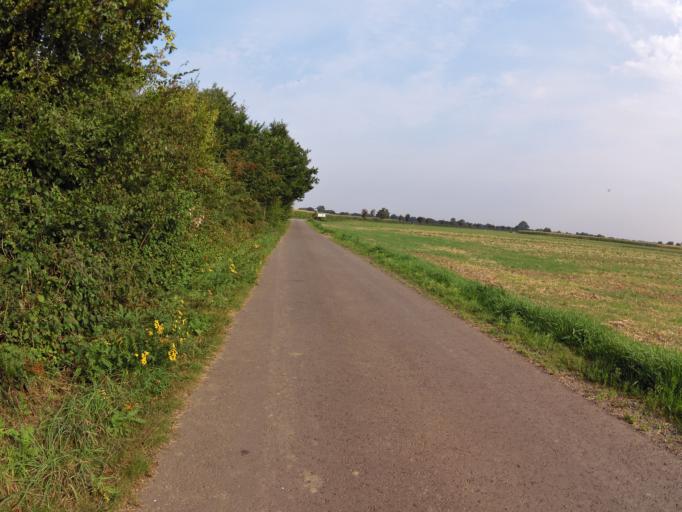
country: DE
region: Lower Saxony
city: Raddestorf
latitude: 52.4649
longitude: 9.0172
